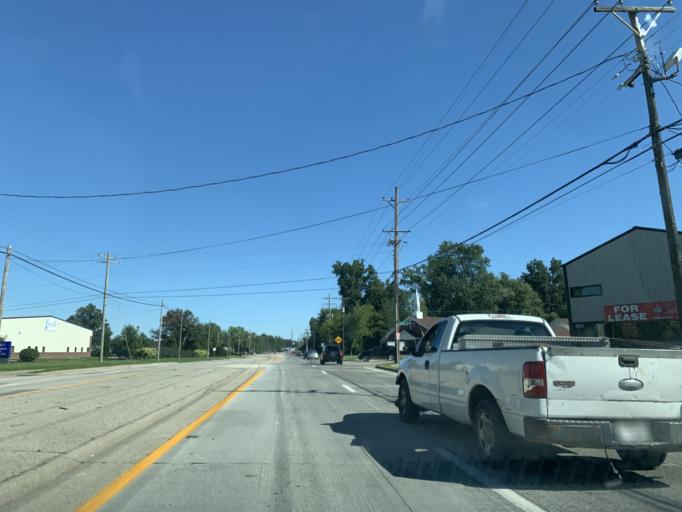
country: US
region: Kentucky
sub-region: Jefferson County
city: Audubon Park
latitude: 38.1818
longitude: -85.6969
